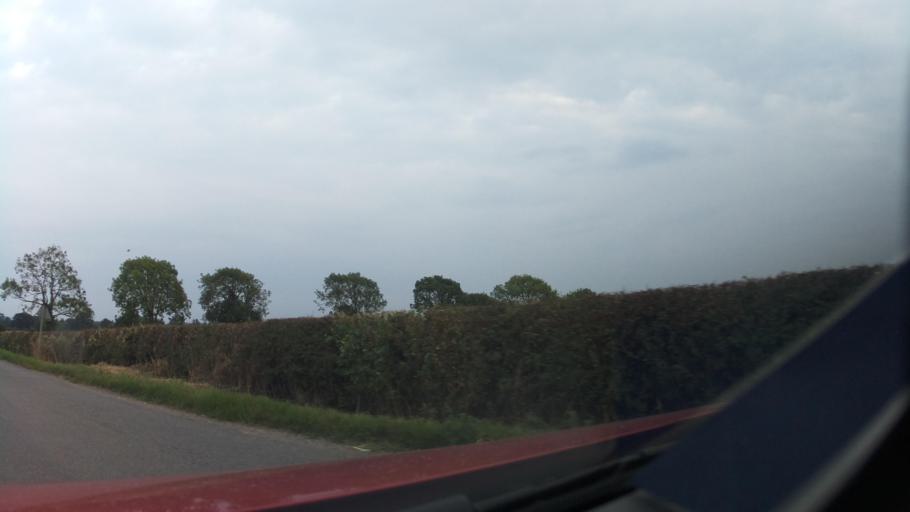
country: GB
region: England
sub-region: Lincolnshire
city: Skellingthorpe
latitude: 53.1430
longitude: -0.6615
